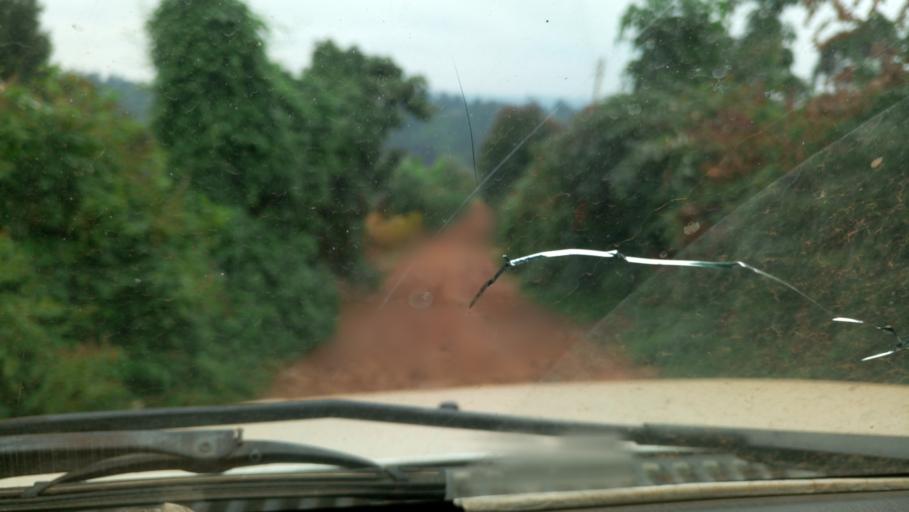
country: KE
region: Murang'a District
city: Kangema
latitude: -0.6846
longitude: 36.9194
